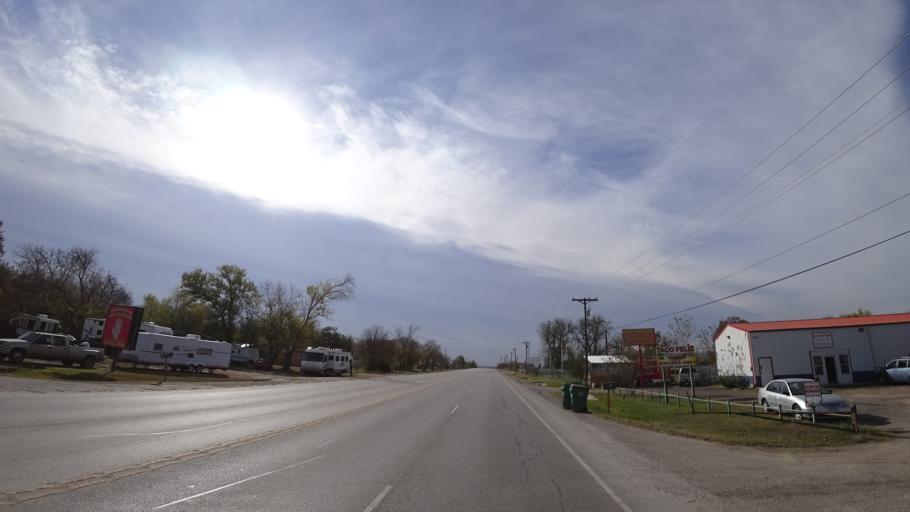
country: US
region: Texas
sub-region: Travis County
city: Onion Creek
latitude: 30.1614
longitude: -97.6939
